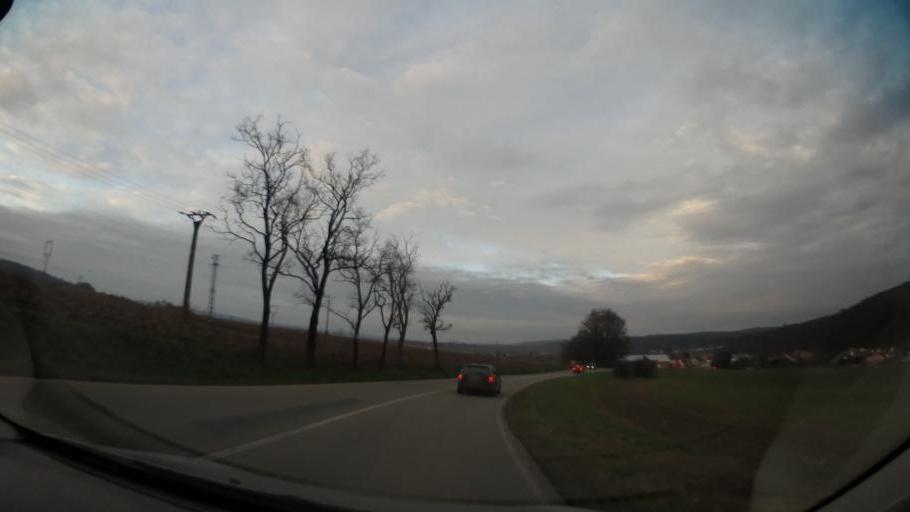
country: CZ
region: South Moravian
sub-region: Okres Brno-Venkov
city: Rosice
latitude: 49.1640
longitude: 16.3941
